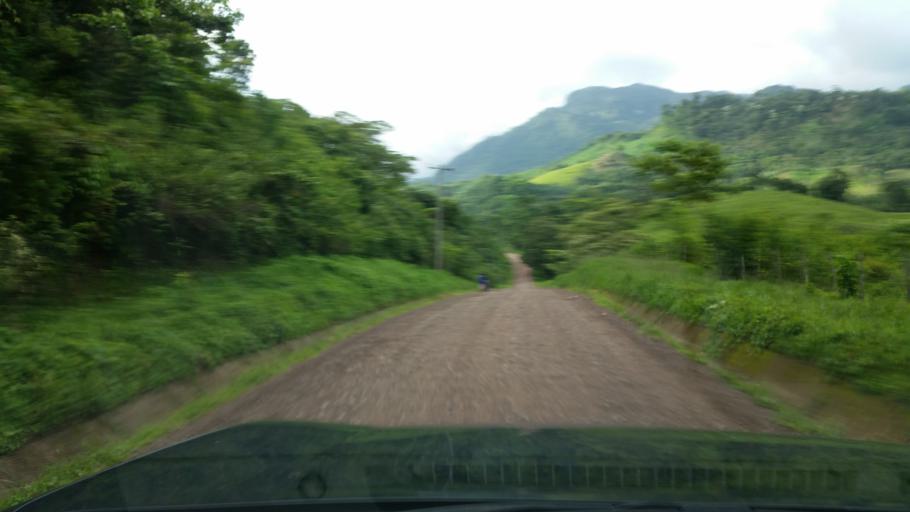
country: NI
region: Jinotega
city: Jinotega
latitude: 13.2265
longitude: -85.7300
